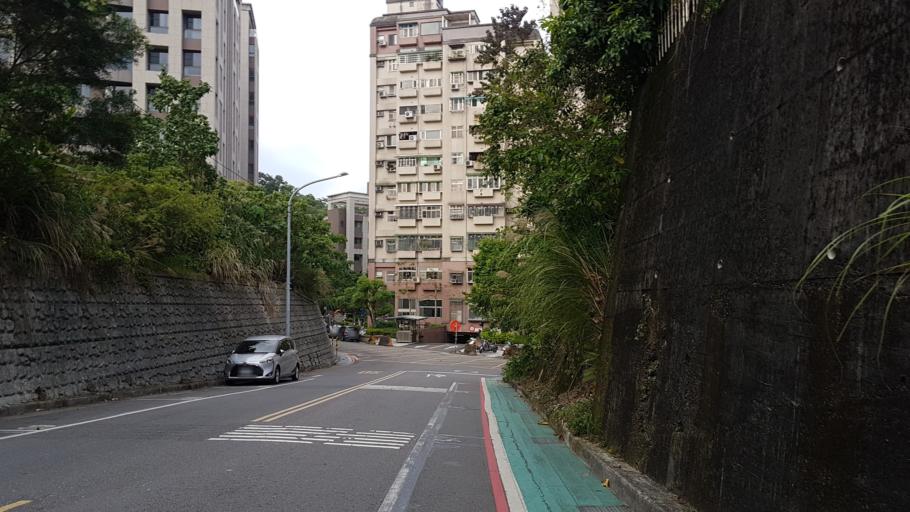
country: TW
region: Taipei
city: Taipei
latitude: 25.0023
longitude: 121.5465
